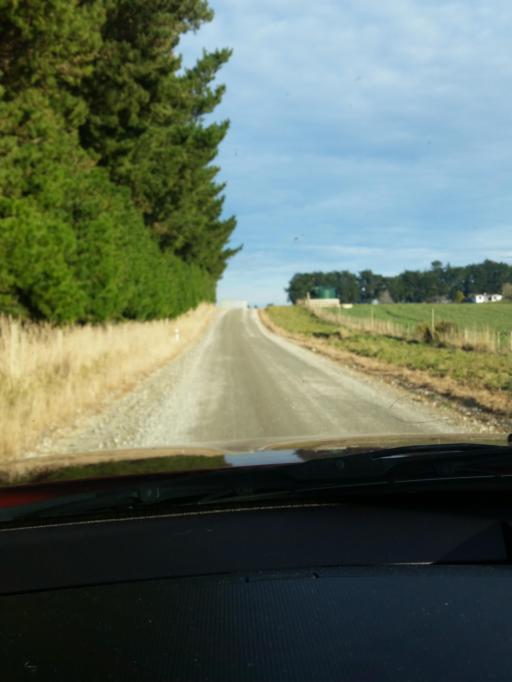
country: NZ
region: Southland
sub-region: Gore District
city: Gore
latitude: -46.2115
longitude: 168.7825
